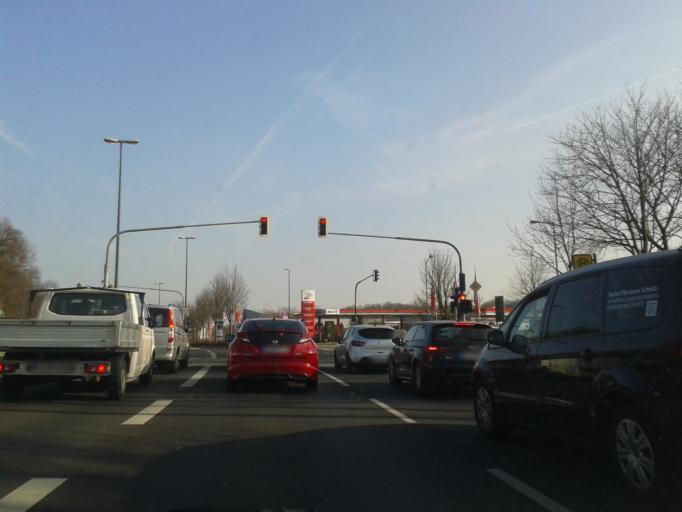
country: DE
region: Saxony
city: Dresden
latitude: 51.0060
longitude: 13.7876
